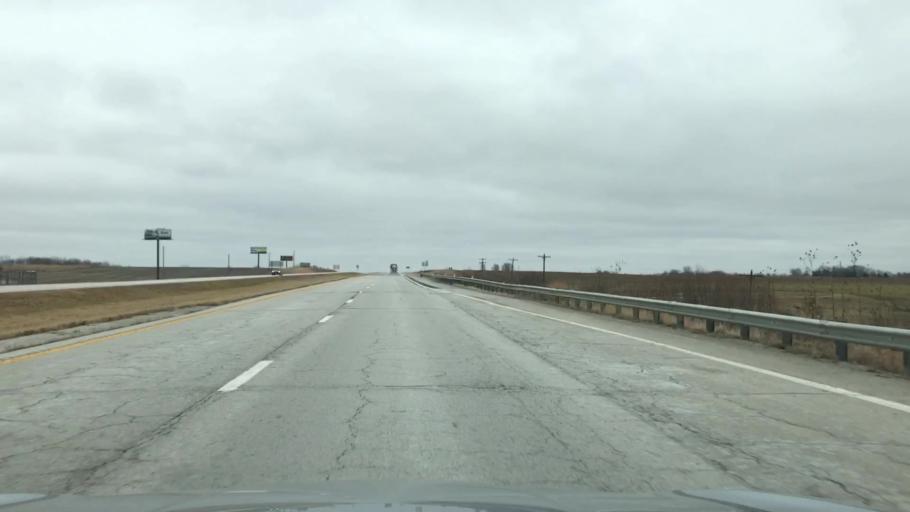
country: US
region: Missouri
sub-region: Caldwell County
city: Hamilton
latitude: 39.7334
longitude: -93.9967
